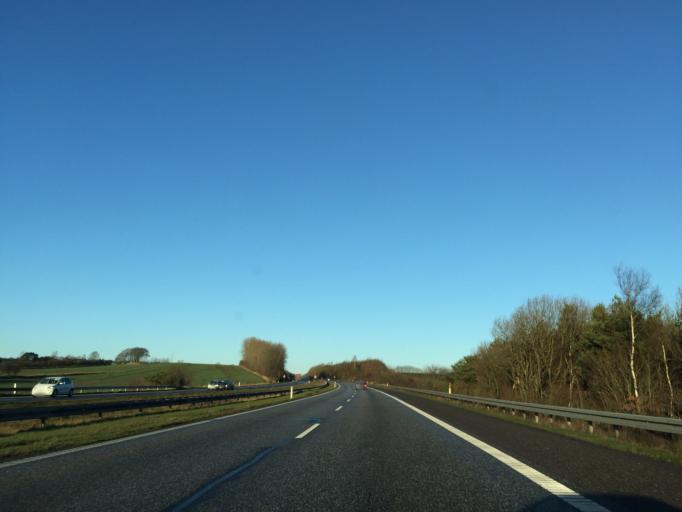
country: DK
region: Central Jutland
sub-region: Skanderborg Kommune
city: Skanderborg
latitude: 56.0173
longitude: 9.8832
